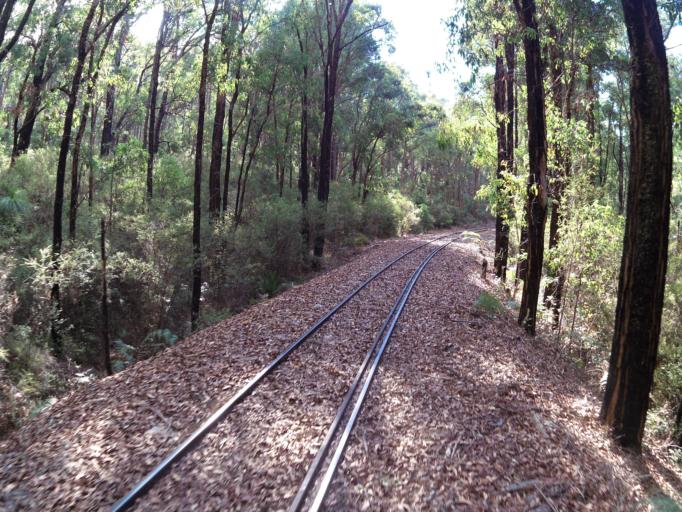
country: AU
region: Western Australia
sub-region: Waroona
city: Waroona
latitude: -32.7347
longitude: 116.1150
